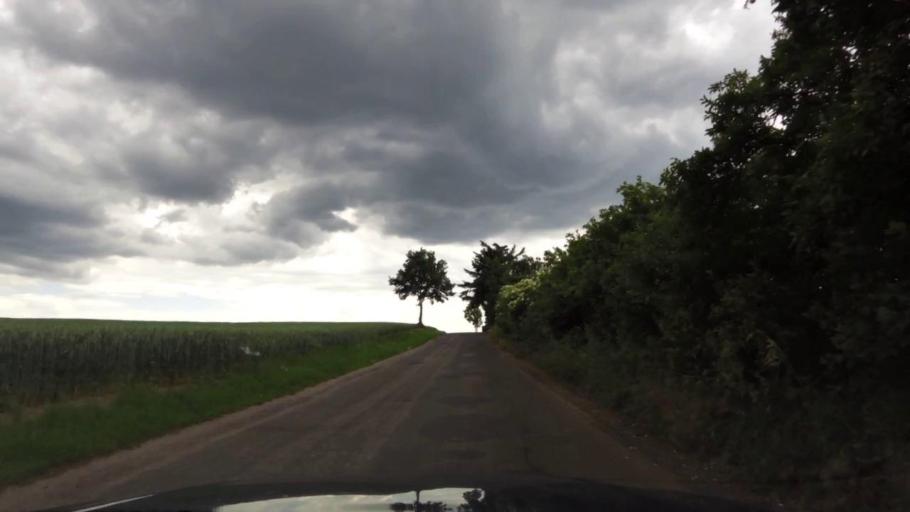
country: PL
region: West Pomeranian Voivodeship
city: Trzcinsko Zdroj
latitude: 52.9228
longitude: 14.5923
